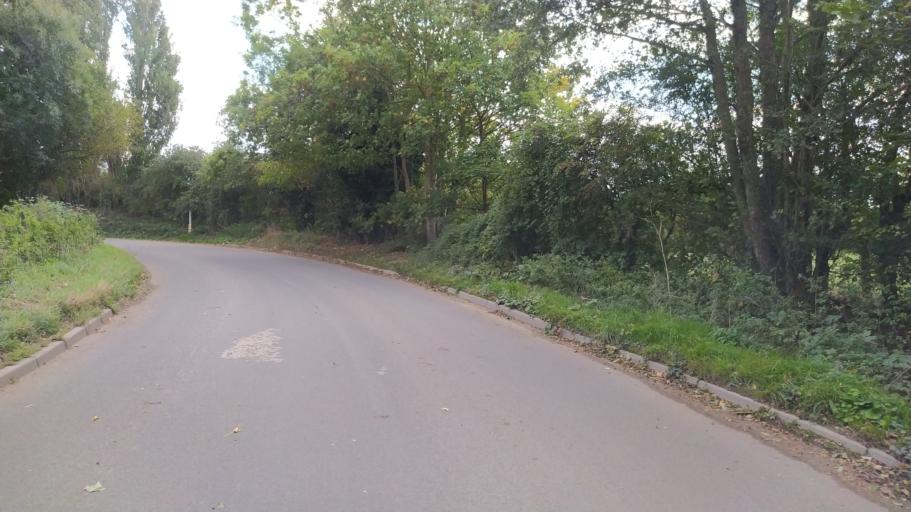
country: GB
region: England
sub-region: West Berkshire
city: Calcot
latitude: 51.4238
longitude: -1.0163
